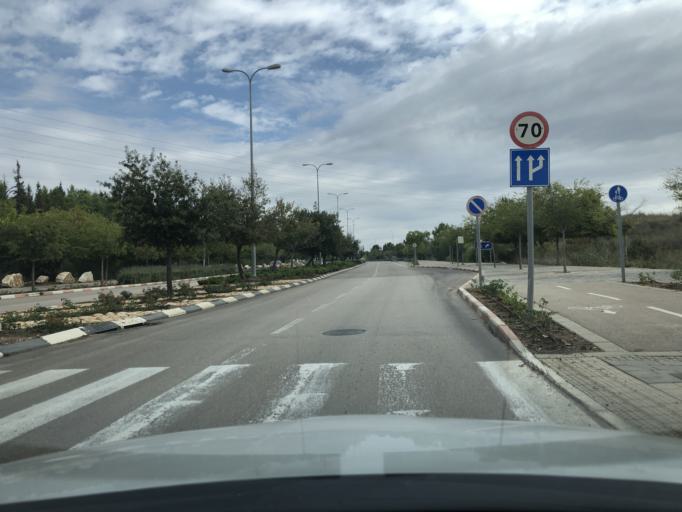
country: PS
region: West Bank
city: Al Midyah
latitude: 31.9235
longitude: 34.9996
